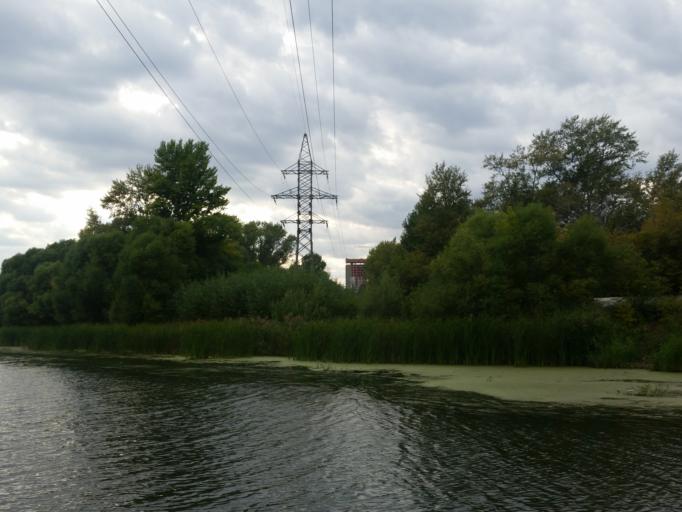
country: RU
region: Ulyanovsk
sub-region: Ulyanovskiy Rayon
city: Ulyanovsk
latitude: 54.3052
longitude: 48.3643
